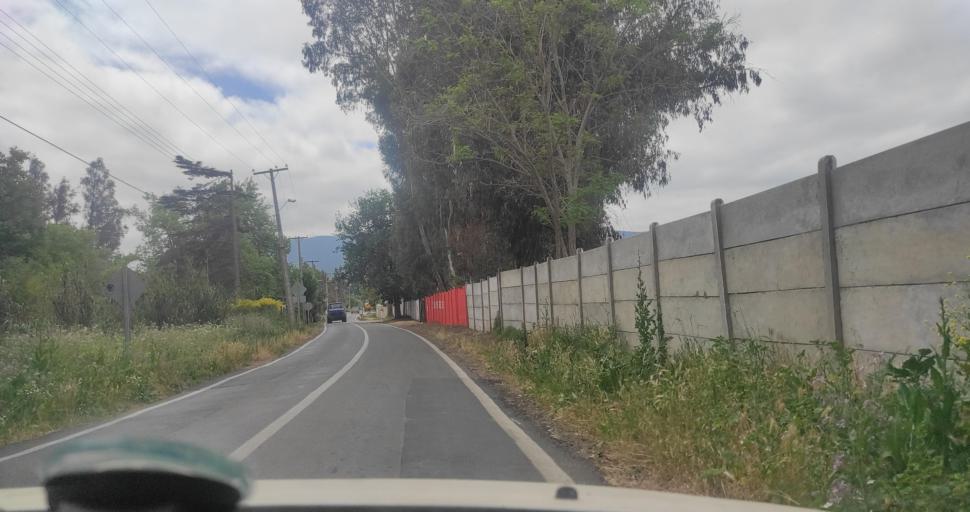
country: CL
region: Valparaiso
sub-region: Provincia de Marga Marga
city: Limache
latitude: -33.0195
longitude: -71.2424
